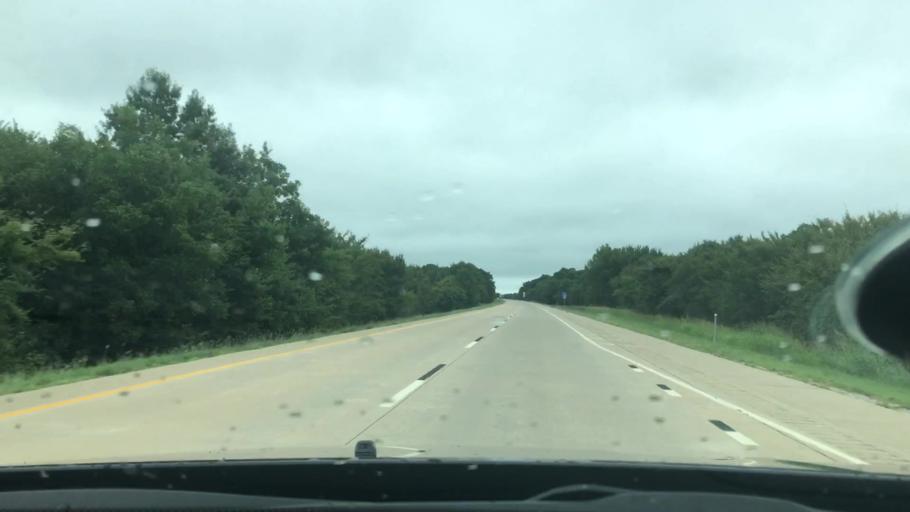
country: US
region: Oklahoma
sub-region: McIntosh County
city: Checotah
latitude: 35.4517
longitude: -95.7106
